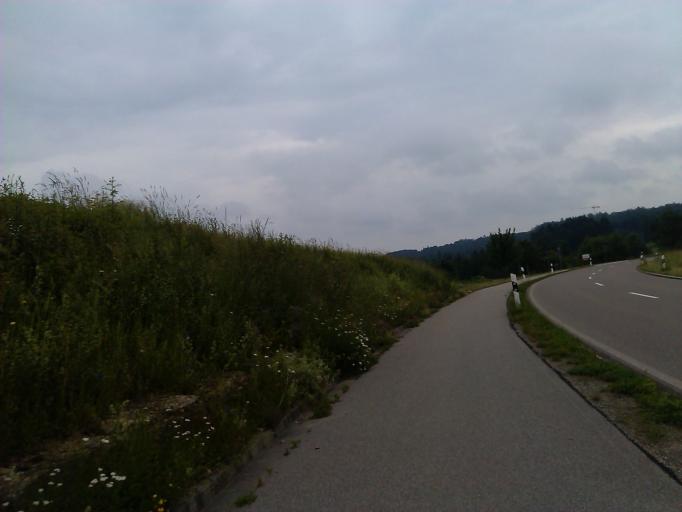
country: DE
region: Baden-Wuerttemberg
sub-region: Regierungsbezirk Stuttgart
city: Mainhardt
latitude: 49.0840
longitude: 9.5298
